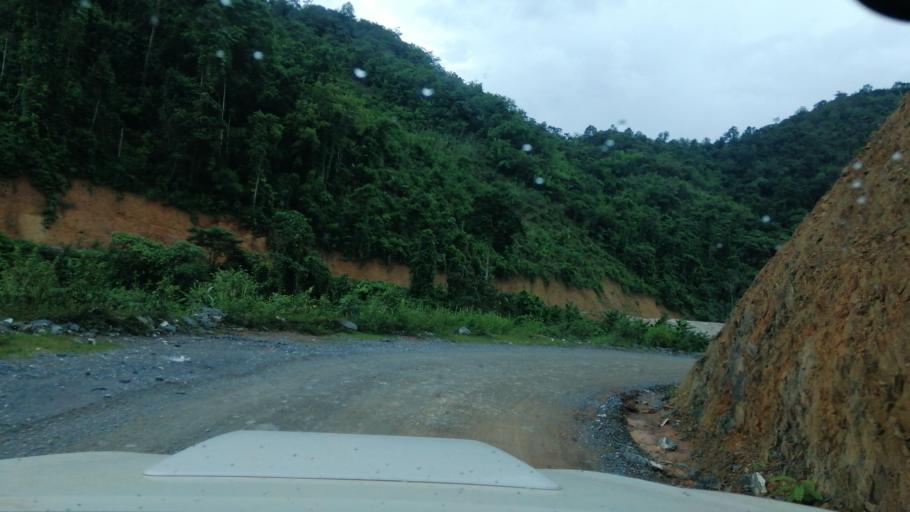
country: LA
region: Xiagnabouli
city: Sainyabuli
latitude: 19.1832
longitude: 101.7962
